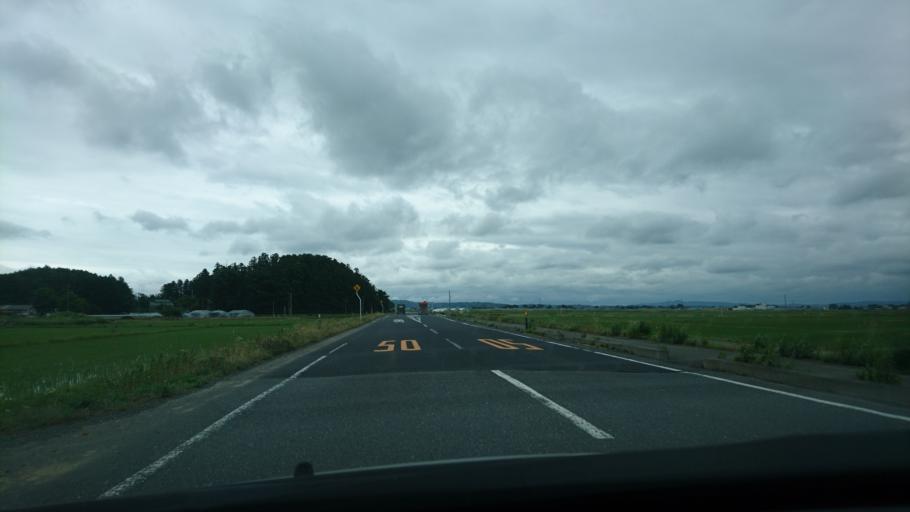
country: JP
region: Miyagi
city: Wakuya
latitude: 38.6978
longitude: 141.2604
